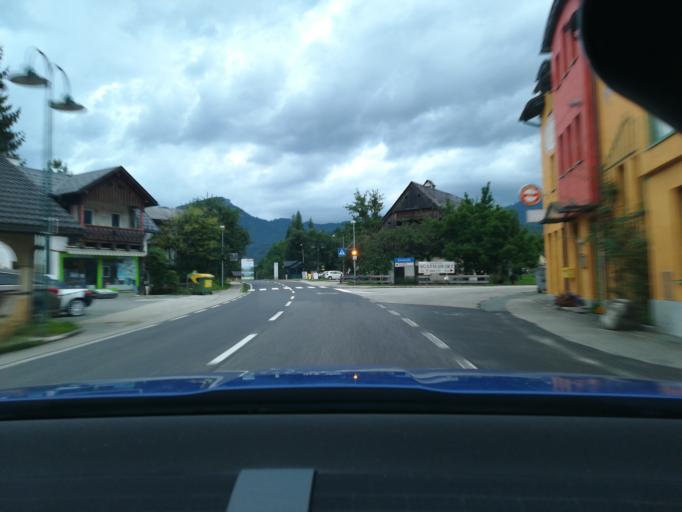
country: AT
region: Upper Austria
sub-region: Politischer Bezirk Gmunden
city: Bad Goisern
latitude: 47.6171
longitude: 13.6348
